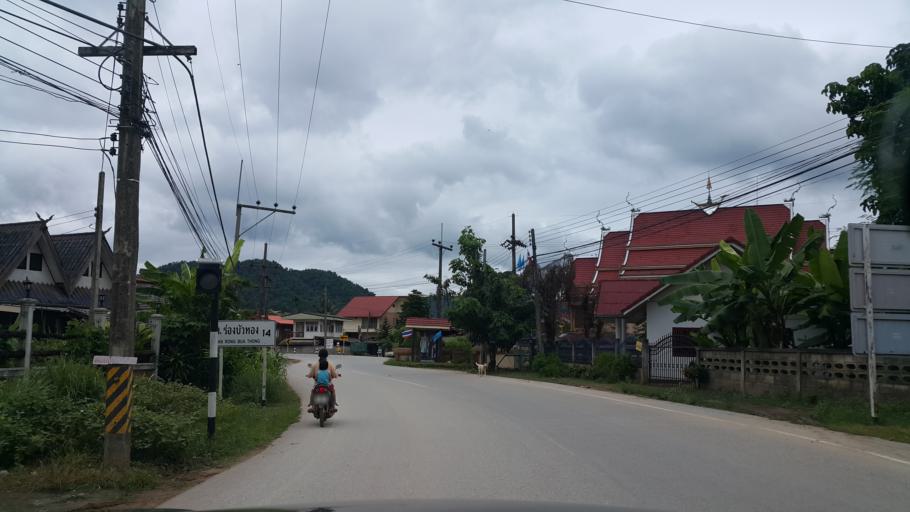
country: TH
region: Chiang Rai
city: Phaya Mengrai
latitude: 19.8914
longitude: 100.1087
